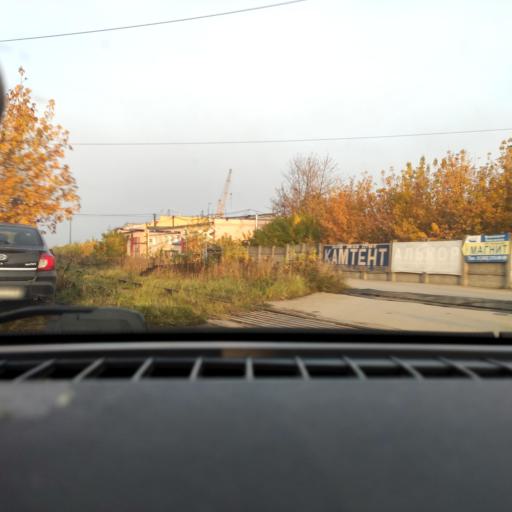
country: RU
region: Perm
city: Kondratovo
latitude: 58.0108
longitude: 56.1664
